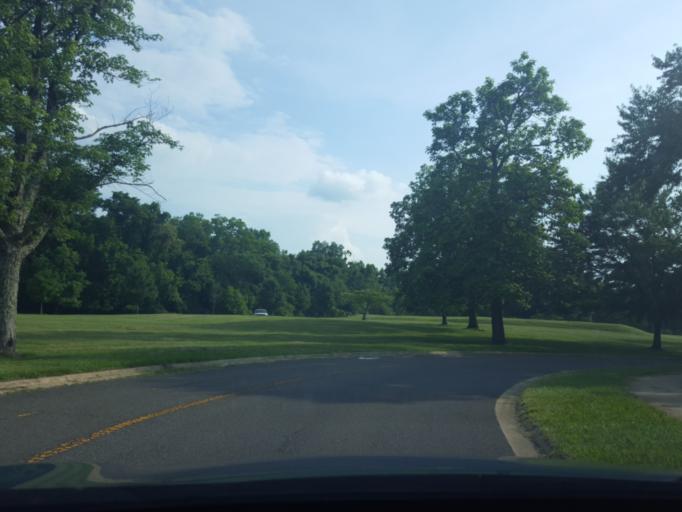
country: US
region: Maryland
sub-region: Prince George's County
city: Fort Washington
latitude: 38.7146
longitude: -77.0285
